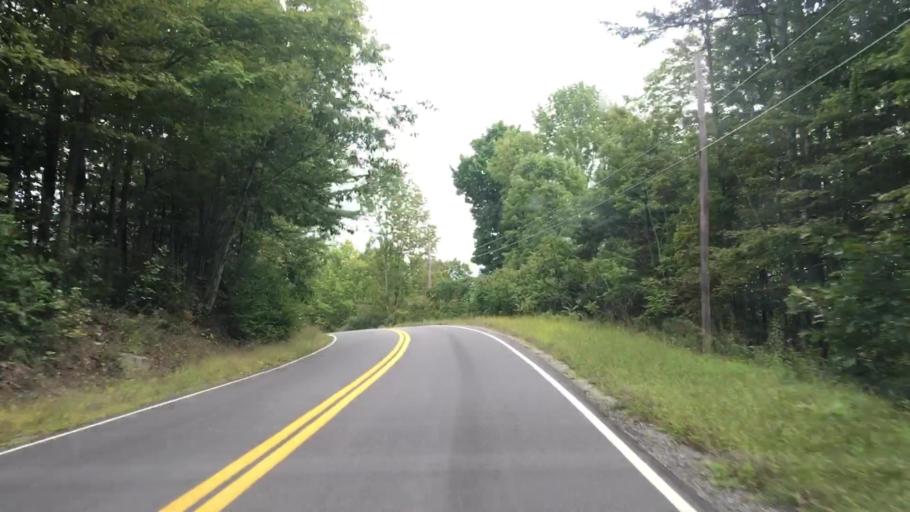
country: US
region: Maine
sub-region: Kennebec County
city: Hallowell
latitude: 44.2644
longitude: -69.8131
